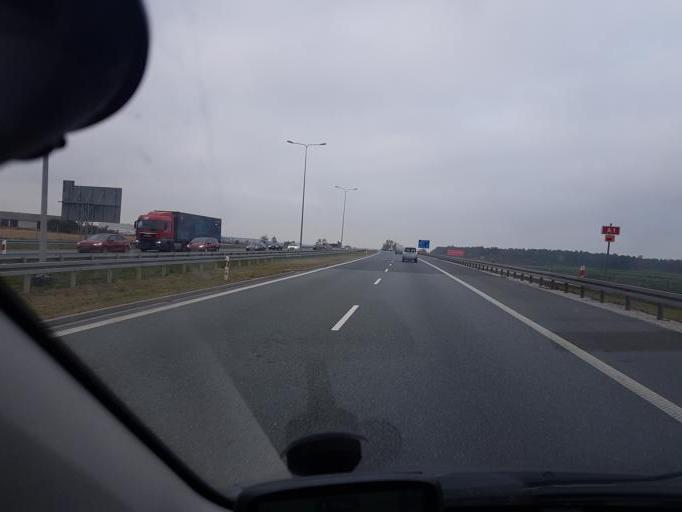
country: PL
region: Kujawsko-Pomorskie
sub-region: Powiat wloclawski
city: Brzesc Kujawski
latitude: 52.6251
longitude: 18.9626
